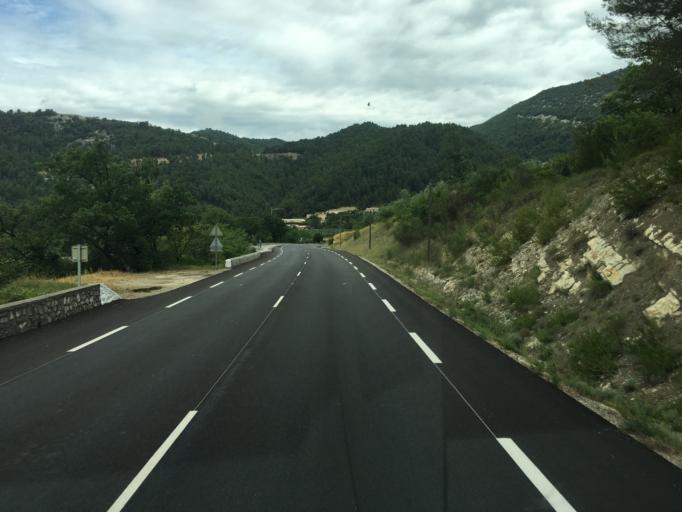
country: FR
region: Rhone-Alpes
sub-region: Departement de la Drome
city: Nyons
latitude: 44.3804
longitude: 5.1807
